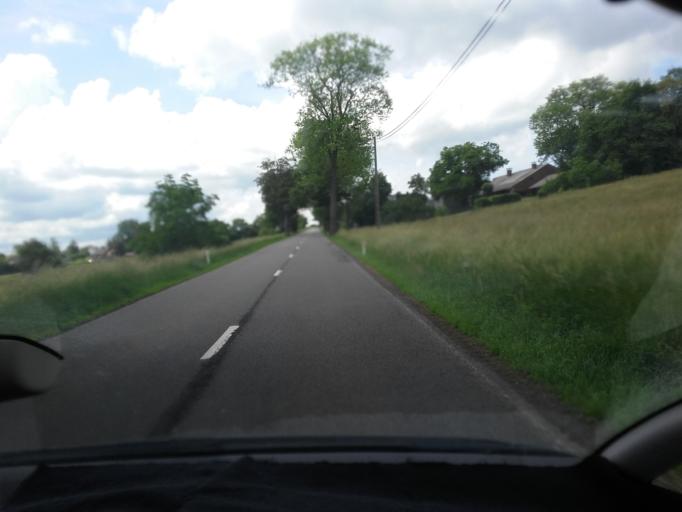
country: BE
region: Wallonia
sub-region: Province de Namur
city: Rochefort
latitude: 50.1259
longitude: 5.2492
